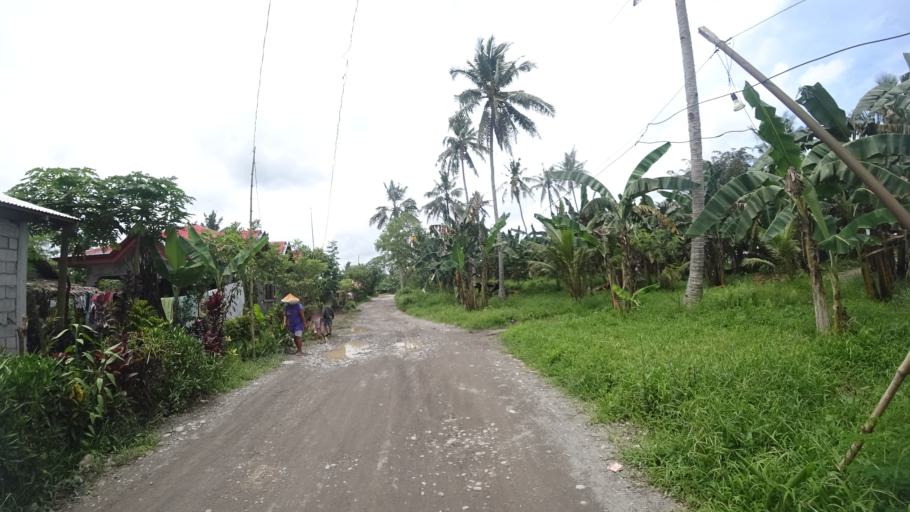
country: PH
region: Eastern Visayas
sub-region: Province of Leyte
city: Jaro
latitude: 11.2042
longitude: 124.8039
